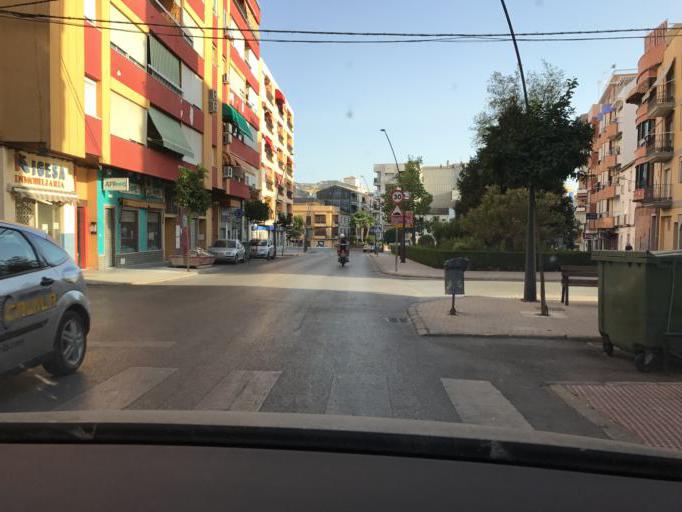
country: ES
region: Andalusia
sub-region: Provincia de Jaen
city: Ubeda
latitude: 38.0158
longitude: -3.3714
